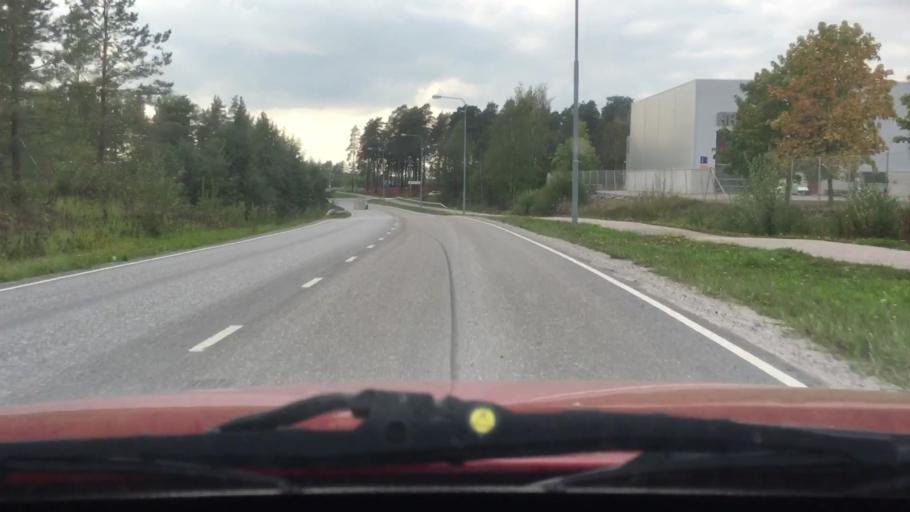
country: FI
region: Varsinais-Suomi
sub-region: Turku
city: Masku
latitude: 60.5490
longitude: 22.1300
